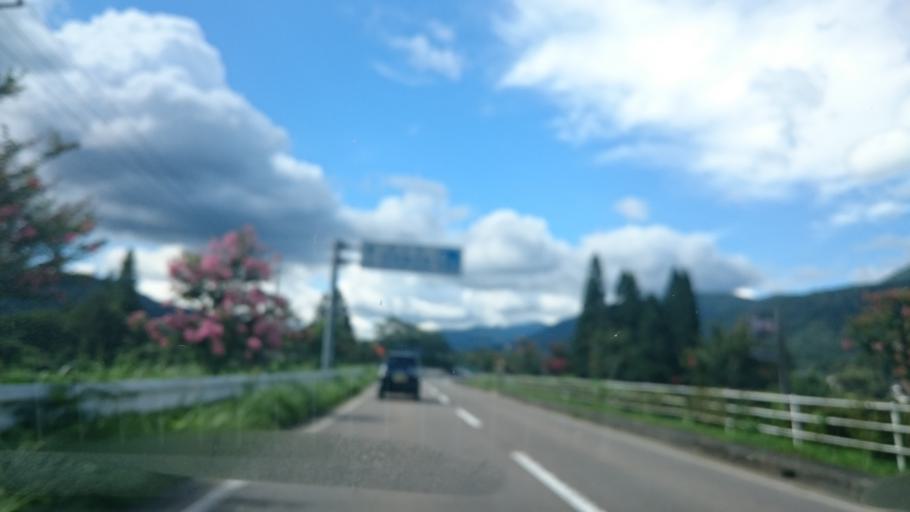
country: JP
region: Gifu
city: Nakatsugawa
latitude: 35.6356
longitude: 137.4460
